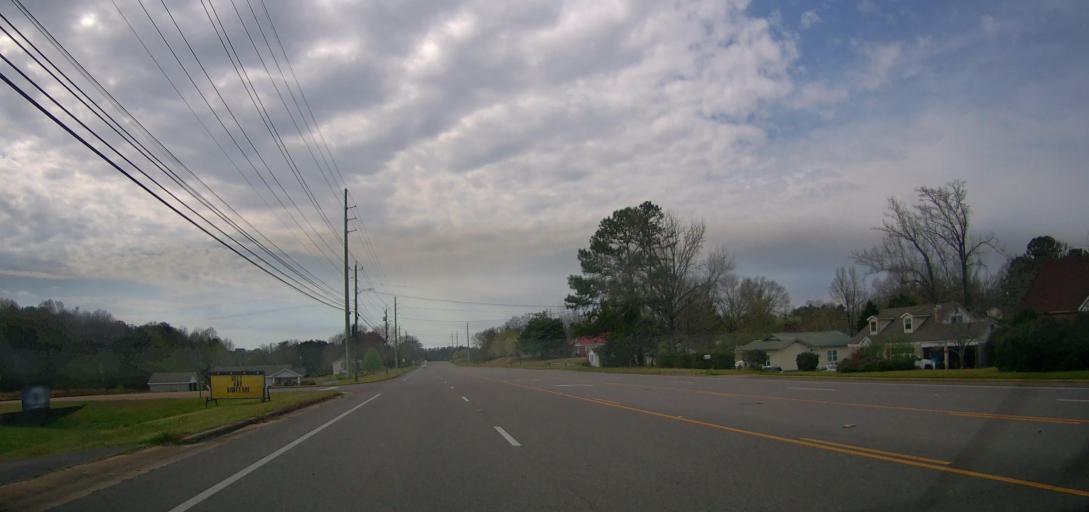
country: US
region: Alabama
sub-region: Marion County
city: Winfield
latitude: 33.9298
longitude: -87.7748
